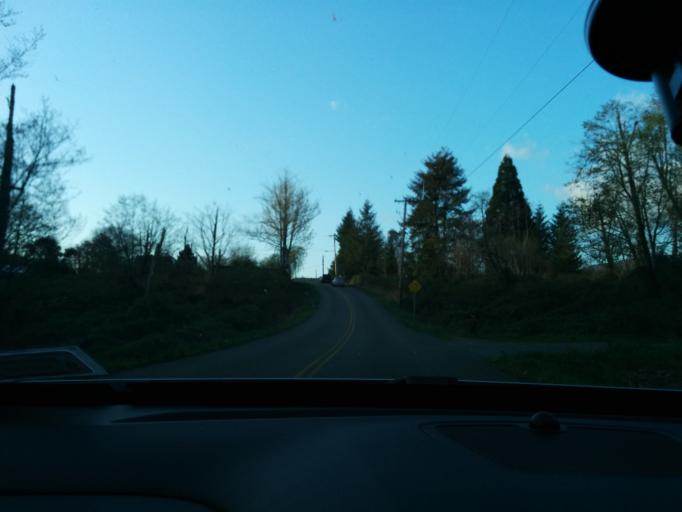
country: US
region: Washington
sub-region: Snohomish County
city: Gold Bar
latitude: 47.8781
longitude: -121.7345
